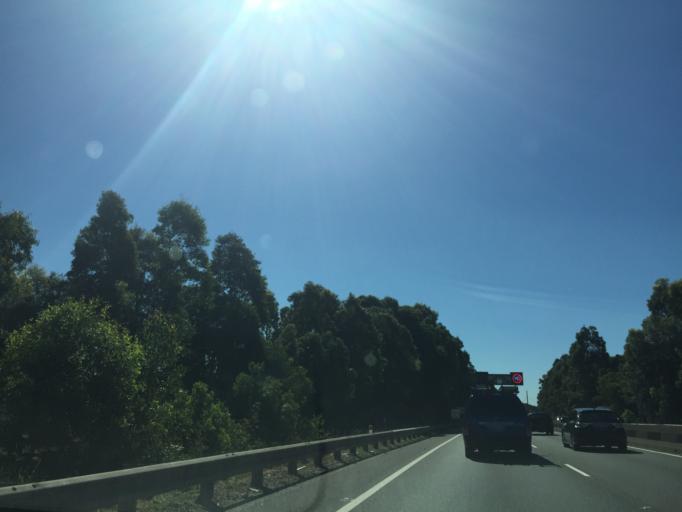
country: AU
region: New South Wales
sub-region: Strathfield
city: Homebush
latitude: -33.8640
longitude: 151.0866
